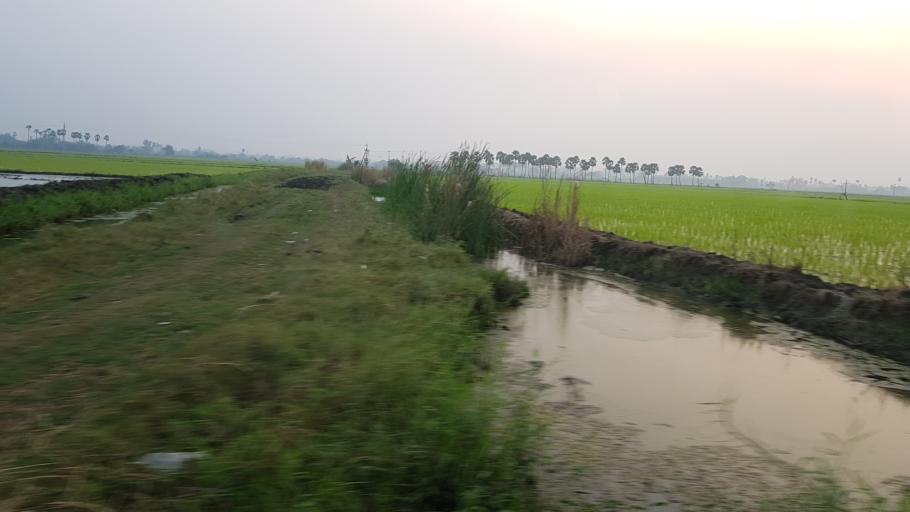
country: IN
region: Andhra Pradesh
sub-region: Krishna
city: Kankipadu
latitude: 16.4566
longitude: 80.7682
